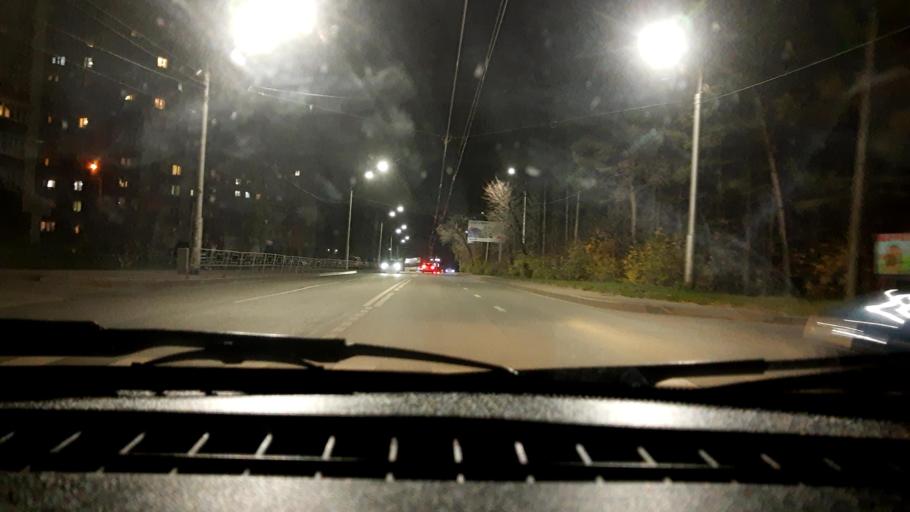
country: RU
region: Bashkortostan
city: Ufa
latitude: 54.6943
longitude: 56.0039
